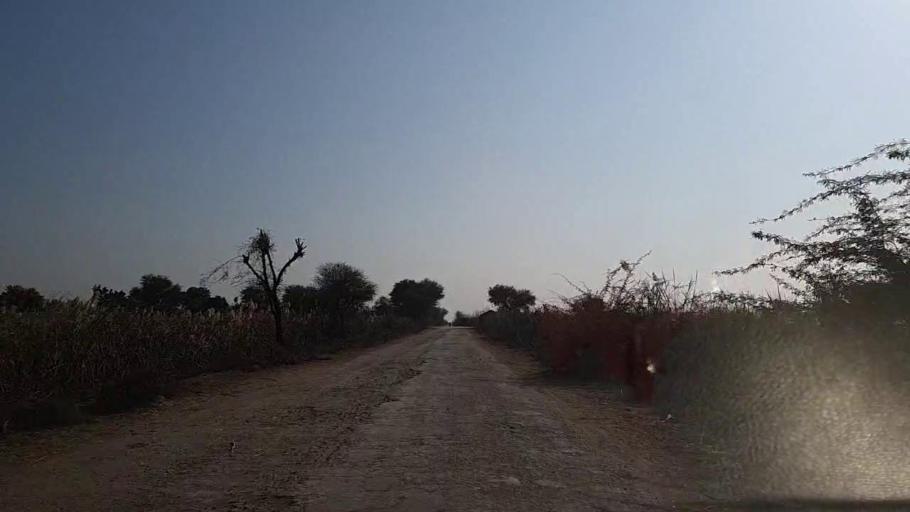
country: PK
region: Sindh
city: Tando Mittha Khan
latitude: 25.8995
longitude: 69.0771
